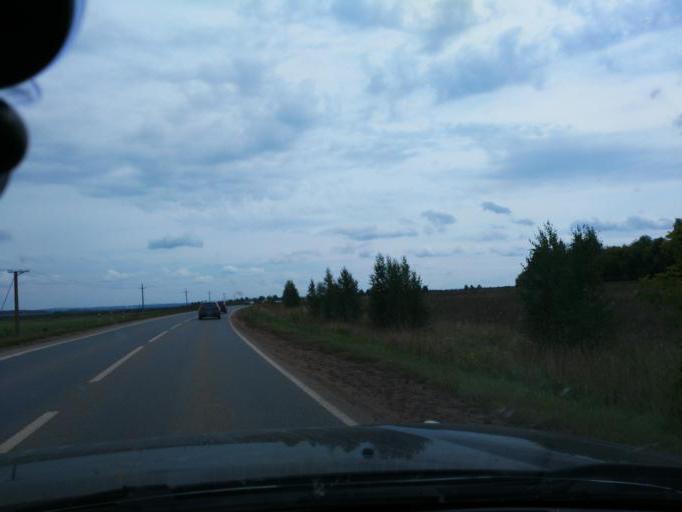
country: RU
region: Perm
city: Chernushka
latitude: 56.5097
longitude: 55.9687
